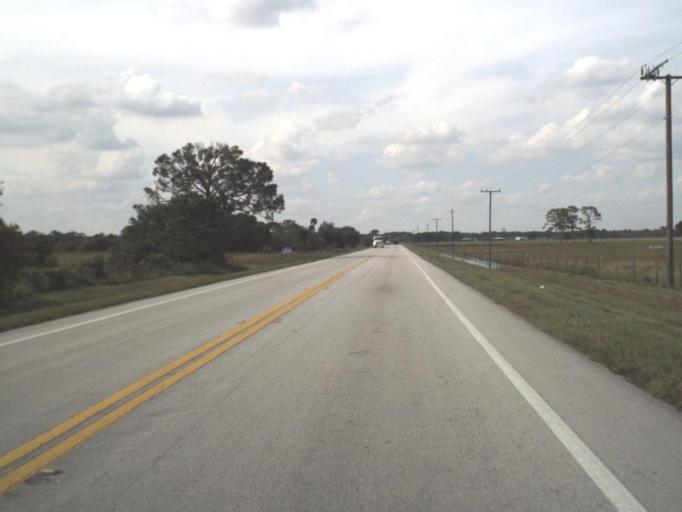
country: US
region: Florida
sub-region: Okeechobee County
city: Taylor Creek
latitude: 27.2211
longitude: -80.7651
